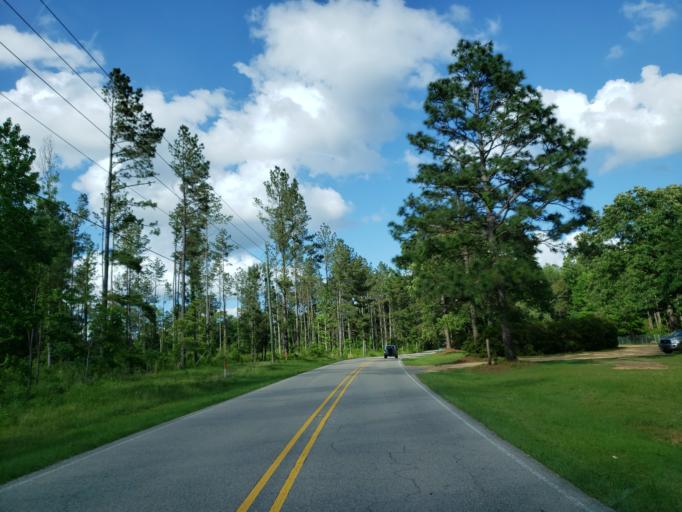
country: US
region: Mississippi
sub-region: Lamar County
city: West Hattiesburg
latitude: 31.2856
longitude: -89.4663
